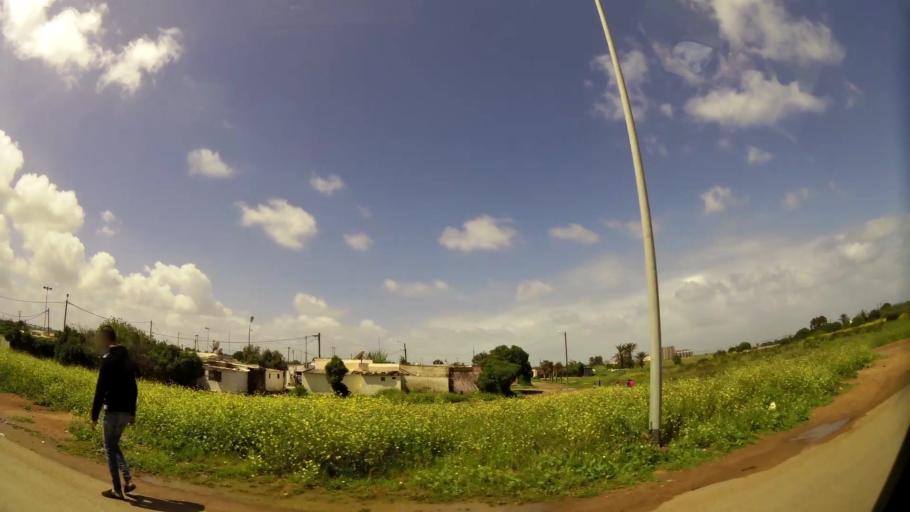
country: MA
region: Grand Casablanca
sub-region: Mediouna
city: Tit Mellil
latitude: 33.6352
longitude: -7.4593
